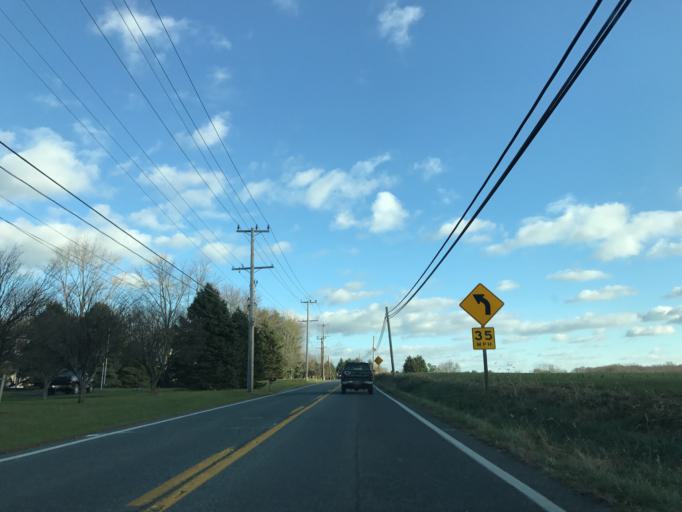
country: US
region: Maryland
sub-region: Harford County
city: Jarrettsville
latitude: 39.6127
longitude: -76.5339
